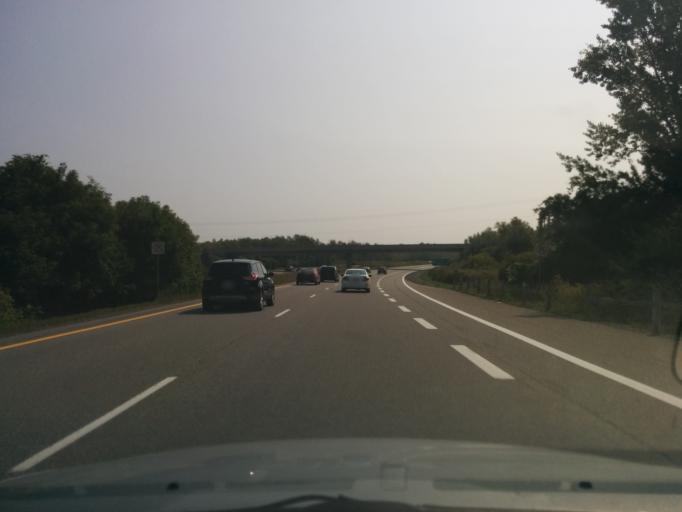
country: CA
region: Ontario
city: Bells Corners
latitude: 45.0818
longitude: -75.6354
